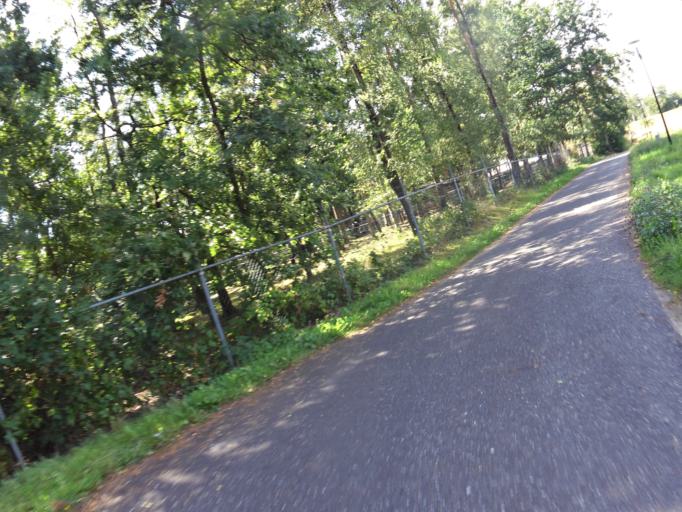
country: NL
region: Limburg
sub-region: Gemeente Heerlen
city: Heerlen
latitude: 50.9072
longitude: 6.0049
